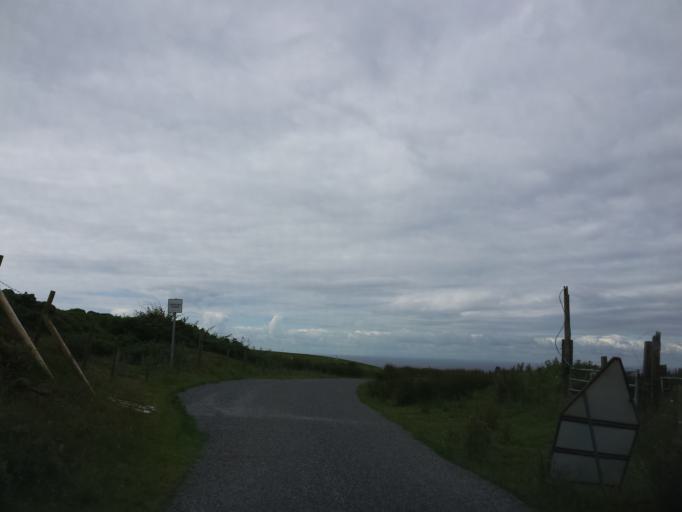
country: GB
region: Scotland
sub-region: Dumfries and Galloway
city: Stranraer
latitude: 54.8692
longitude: -5.1270
